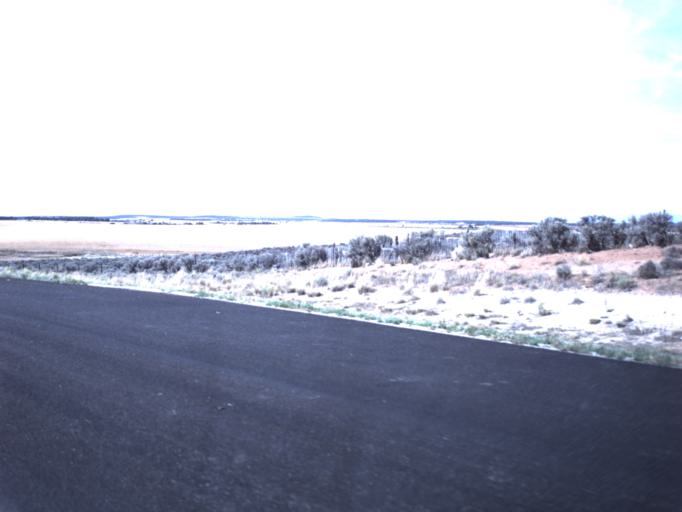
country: US
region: Colorado
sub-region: Dolores County
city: Dove Creek
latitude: 37.8173
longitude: -109.0447
